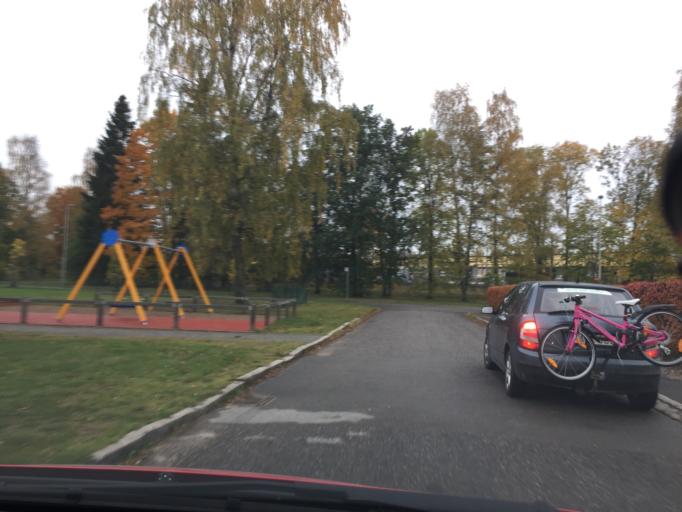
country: SE
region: Vaestra Goetaland
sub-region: Trollhattan
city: Trollhattan
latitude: 58.2812
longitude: 12.3133
